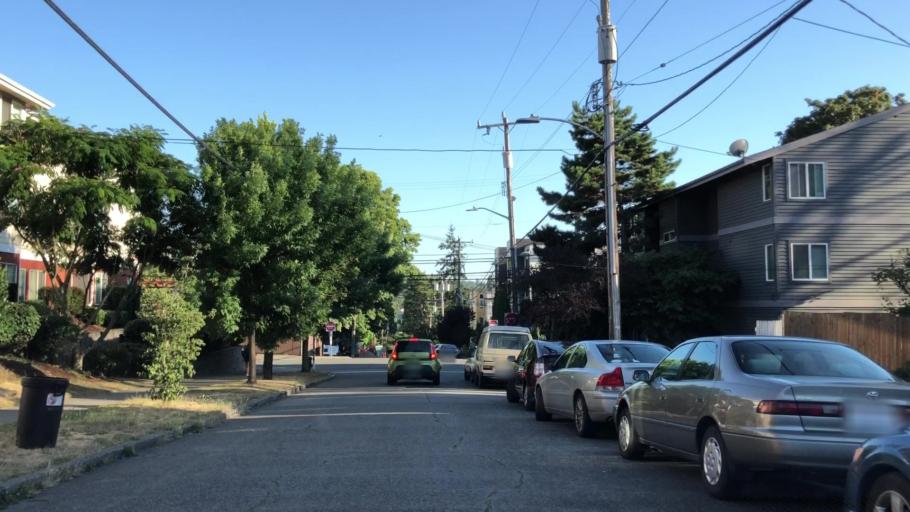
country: US
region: Washington
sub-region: King County
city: Seattle
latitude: 47.6581
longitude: -122.3198
